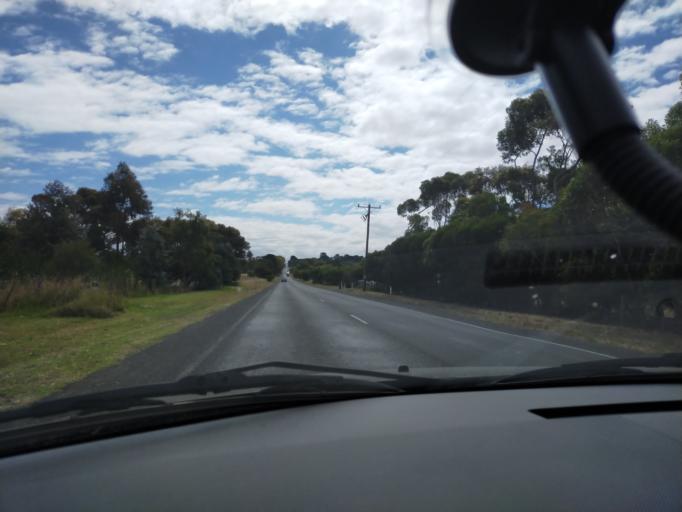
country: AU
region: Victoria
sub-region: Greater Geelong
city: Breakwater
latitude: -38.2497
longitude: 144.3424
